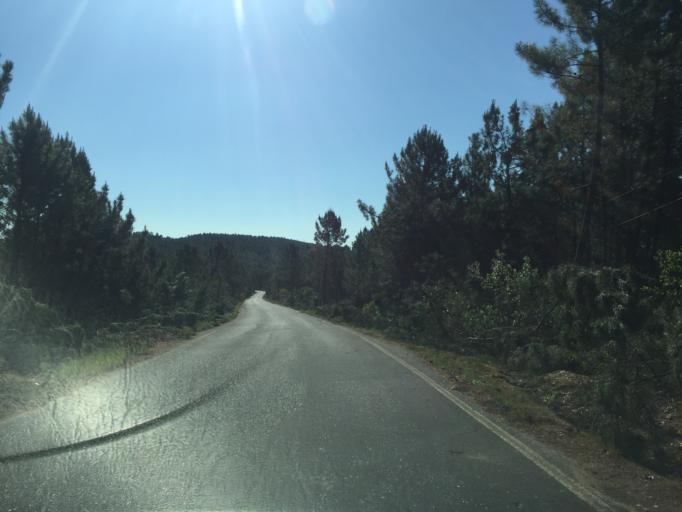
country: PT
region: Coimbra
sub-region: Pampilhosa da Serra
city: Pampilhosa da Serra
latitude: 40.0515
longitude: -7.8381
